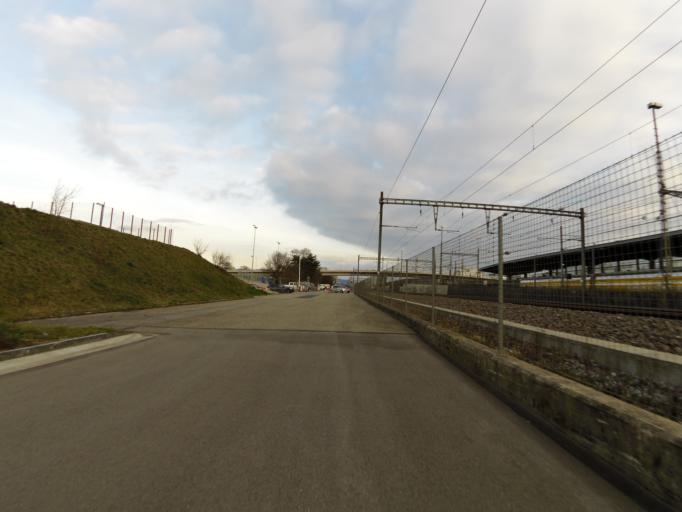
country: CH
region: Zurich
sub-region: Bezirk Dietikon
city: Oberengstringen
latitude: 47.3967
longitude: 8.4710
